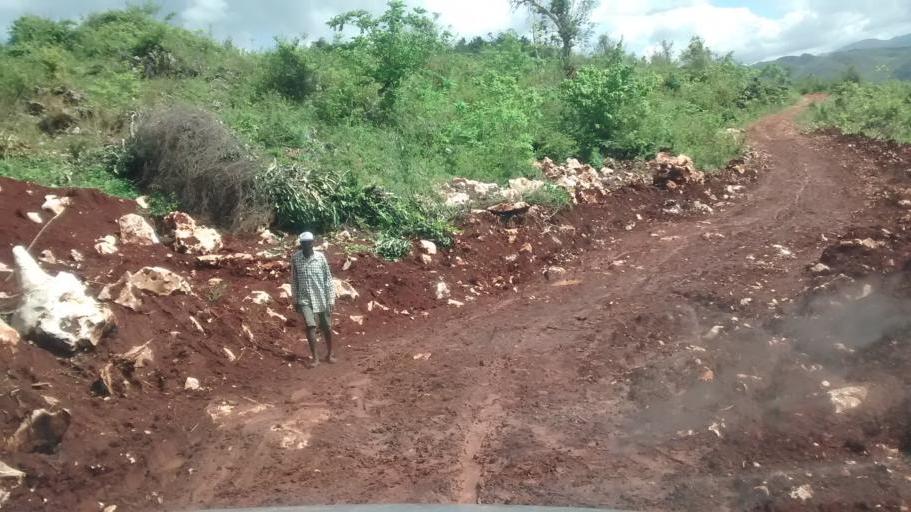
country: HT
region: Grandans
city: Corail
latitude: 18.5405
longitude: -73.9229
